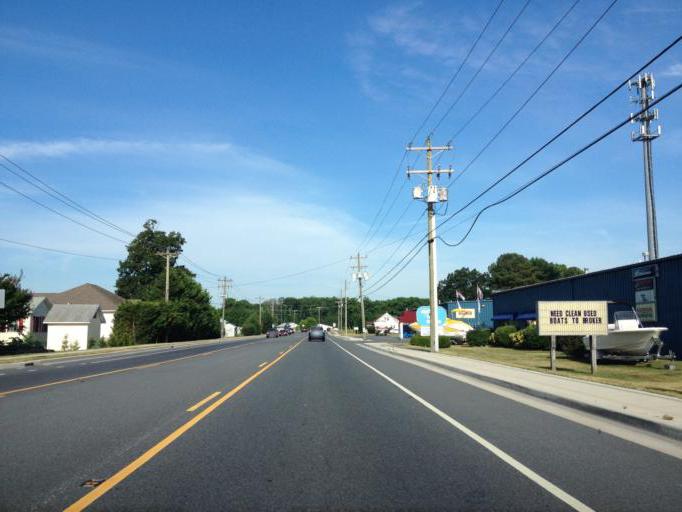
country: US
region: Delaware
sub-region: Sussex County
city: Ocean View
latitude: 38.4728
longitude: -75.1077
